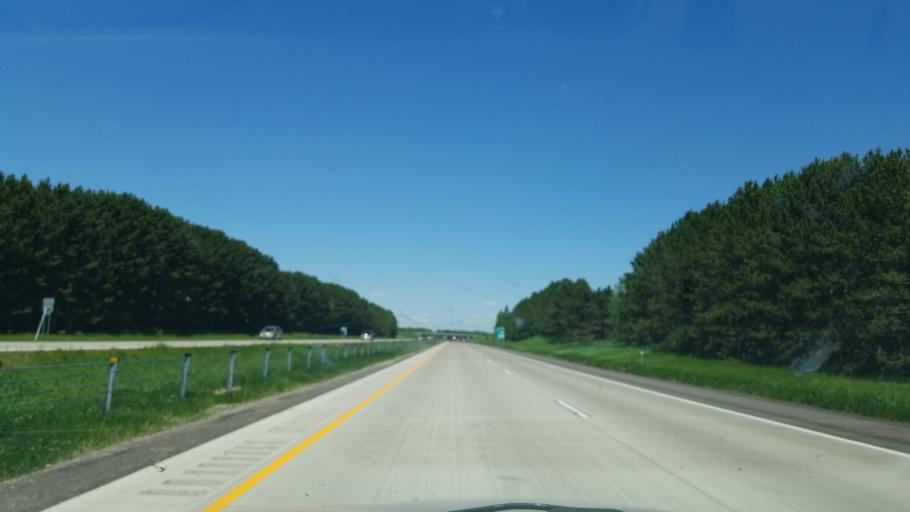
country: US
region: Minnesota
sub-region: Pine County
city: Hinckley
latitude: 45.9694
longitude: -92.9575
